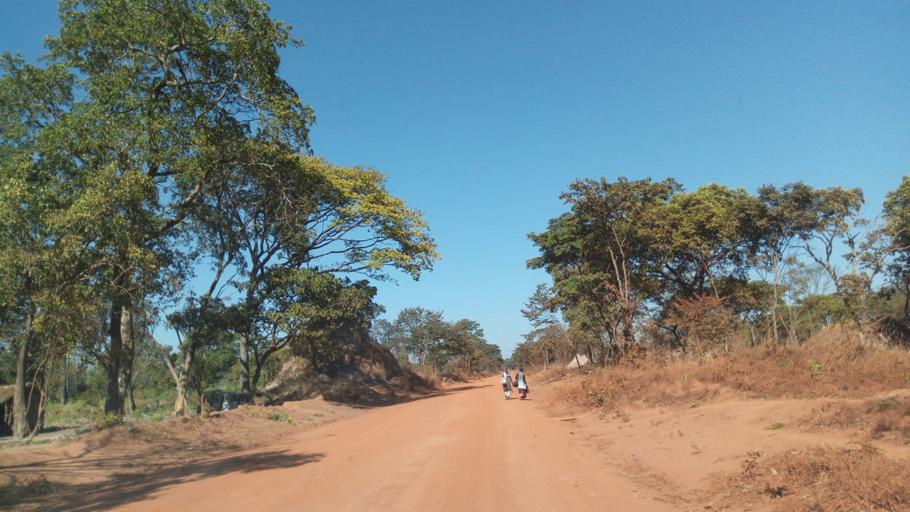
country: ZM
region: Luapula
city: Mwense
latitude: -10.6760
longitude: 28.4065
